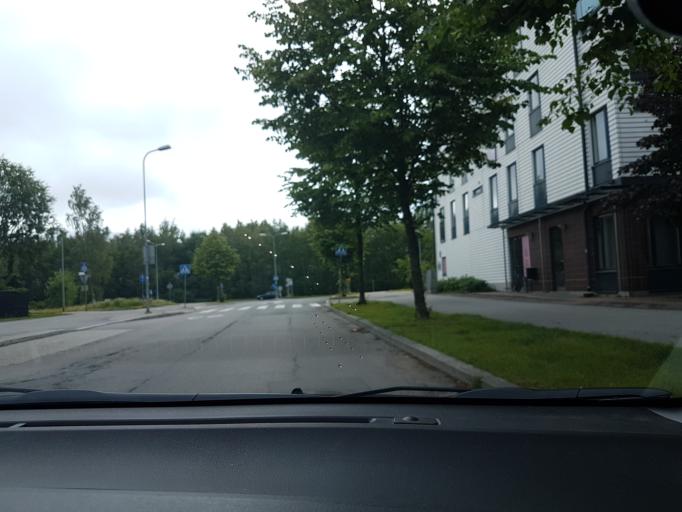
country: FI
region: Uusimaa
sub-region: Helsinki
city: Vantaa
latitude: 60.2628
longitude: 25.0395
